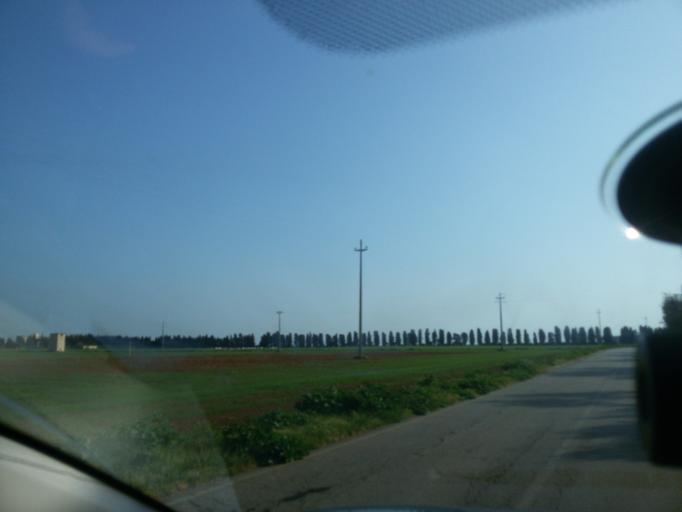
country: IT
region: Apulia
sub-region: Provincia di Brindisi
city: Mesagne
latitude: 40.6005
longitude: 17.8174
